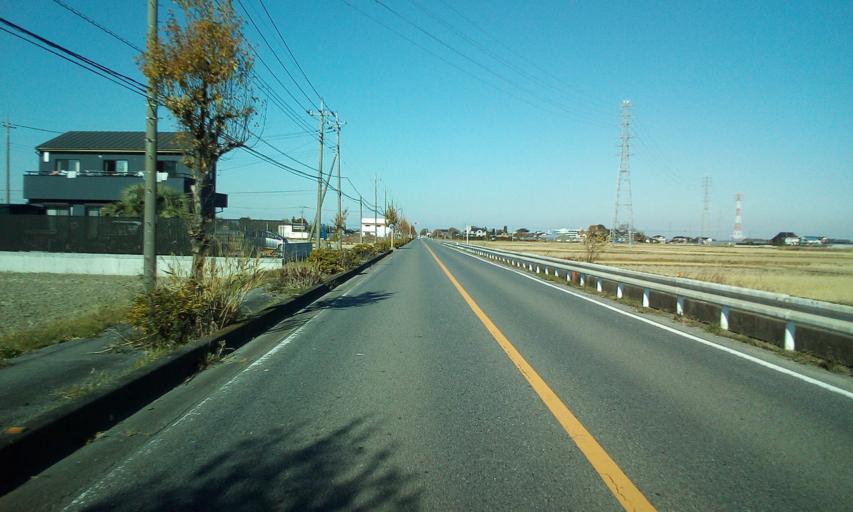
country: JP
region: Saitama
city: Kasukabe
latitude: 36.0139
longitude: 139.7924
